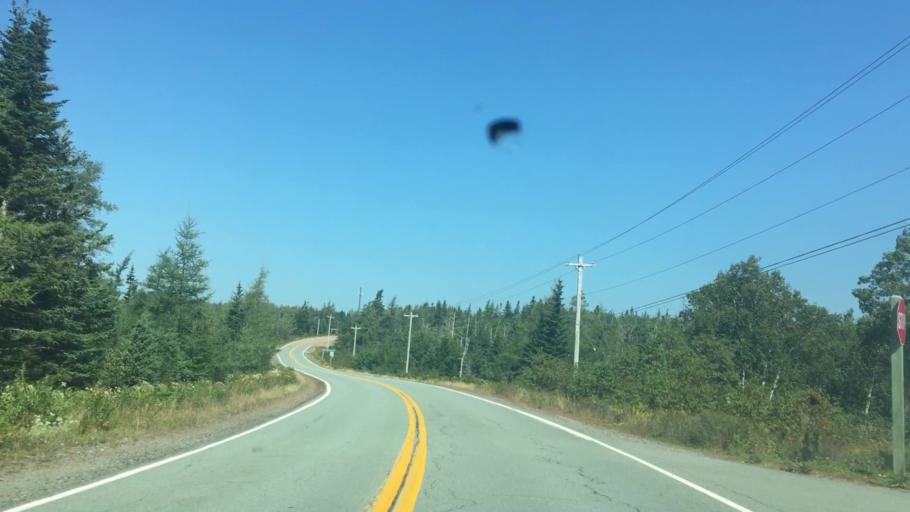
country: CA
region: Nova Scotia
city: Antigonish
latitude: 45.0216
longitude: -62.0312
